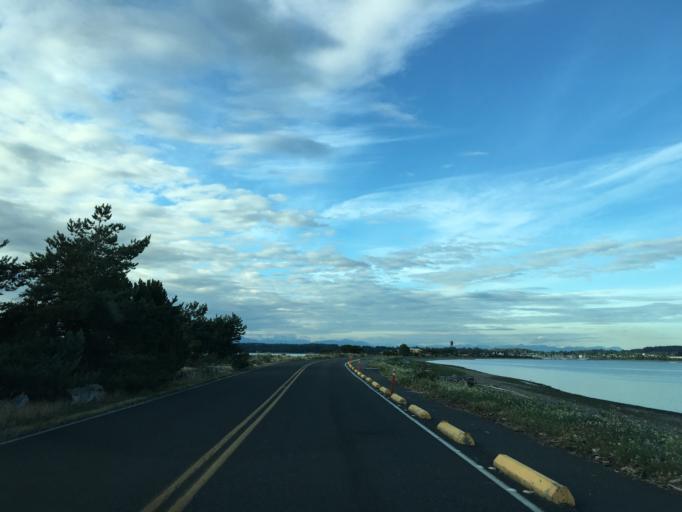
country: CA
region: British Columbia
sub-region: Greater Vancouver Regional District
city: White Rock
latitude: 48.9798
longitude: -122.7893
